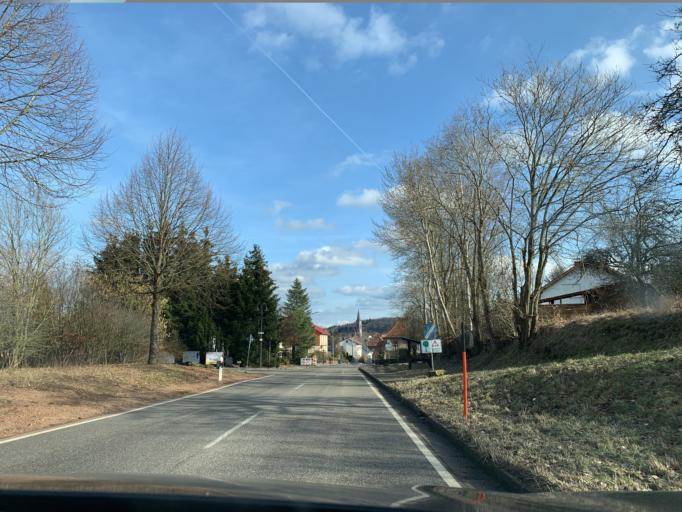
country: DE
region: Rheinland-Pfalz
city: Clausen
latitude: 49.2618
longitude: 7.6656
